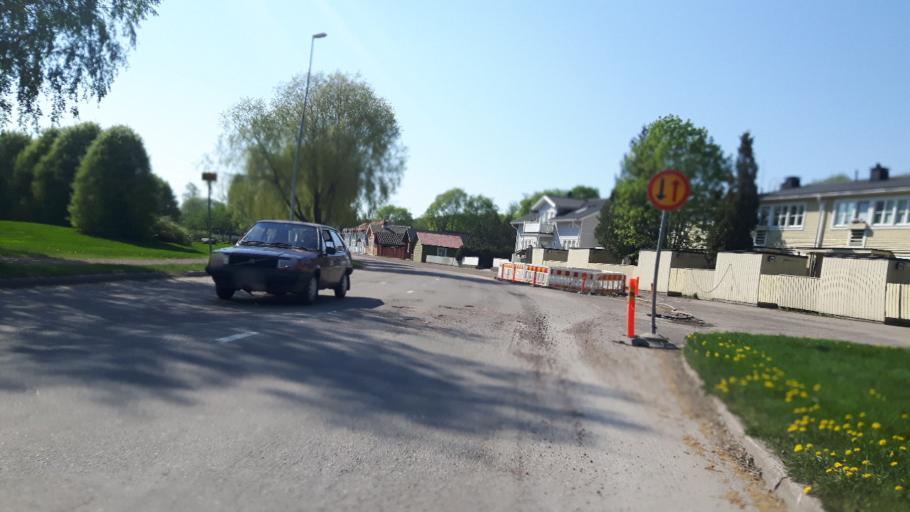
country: FI
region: Uusimaa
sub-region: Loviisa
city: Lovisa
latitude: 60.4546
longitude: 26.2322
